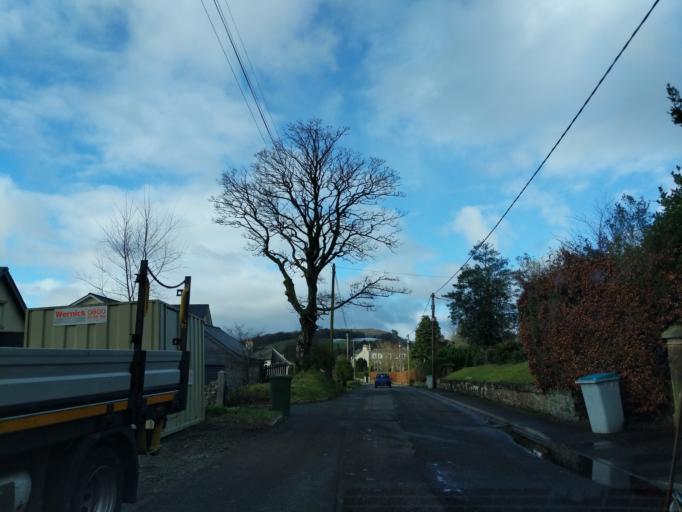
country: GB
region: Scotland
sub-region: Dumfries and Galloway
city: Moffat
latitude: 55.3281
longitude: -3.4320
